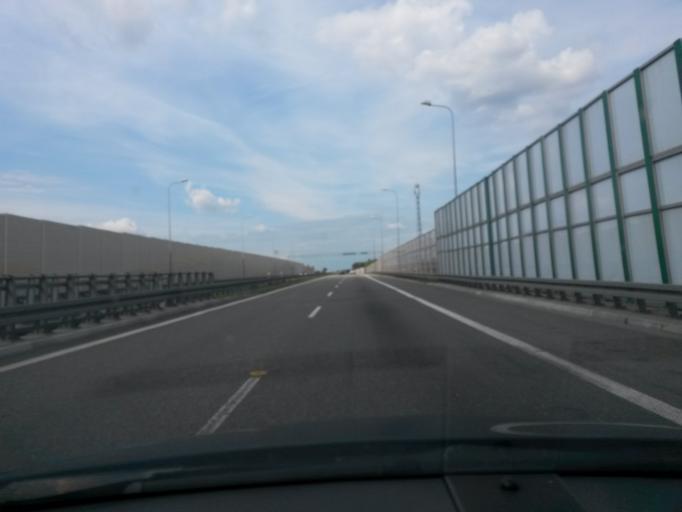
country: PL
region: Lodz Voivodeship
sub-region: Powiat skierniewicki
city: Kowiesy
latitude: 51.8892
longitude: 20.4192
